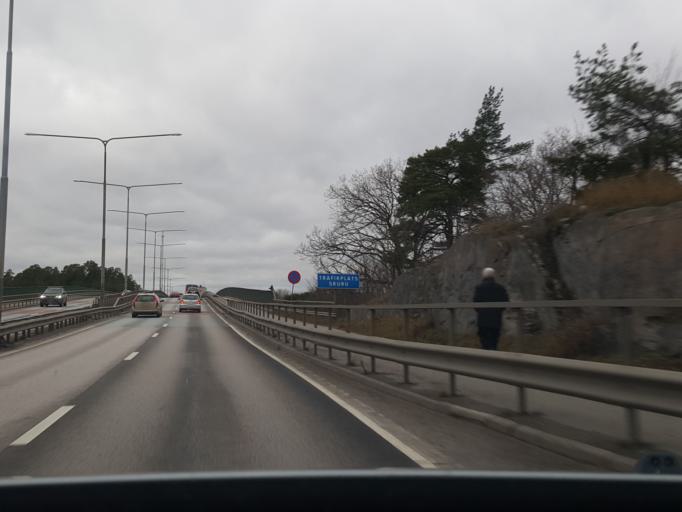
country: SE
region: Stockholm
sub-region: Lidingo
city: Brevik
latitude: 59.3143
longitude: 18.2250
